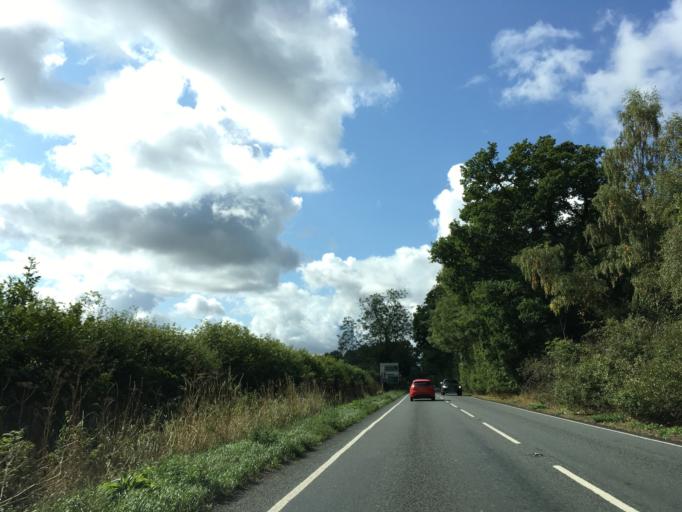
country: GB
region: England
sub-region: Hampshire
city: Highclere
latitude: 51.3502
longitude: -1.3358
